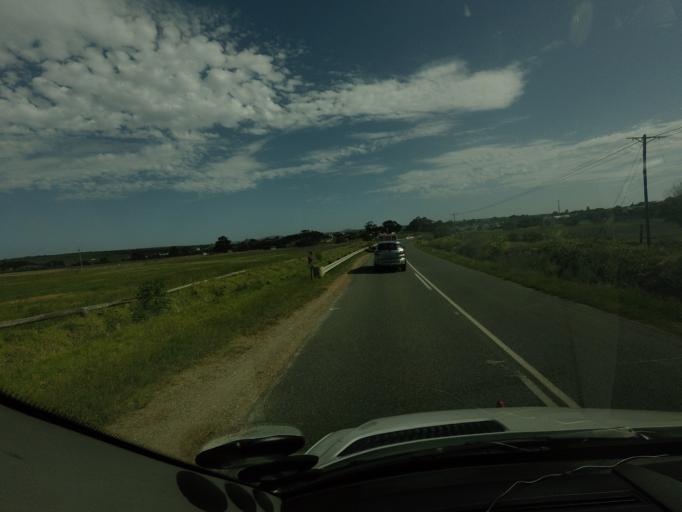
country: ZA
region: Western Cape
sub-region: Overberg District Municipality
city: Caledon
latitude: -34.4317
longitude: 19.4635
